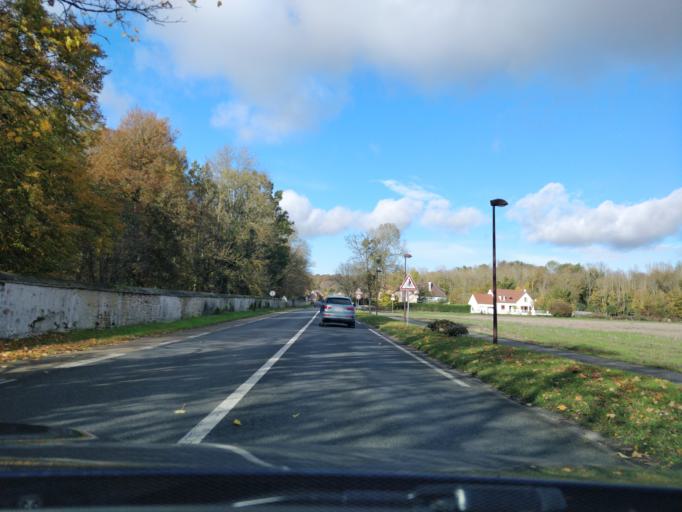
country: FR
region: Ile-de-France
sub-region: Departement de l'Essonne
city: Fontenay-les-Briis
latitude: 48.6158
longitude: 2.1596
